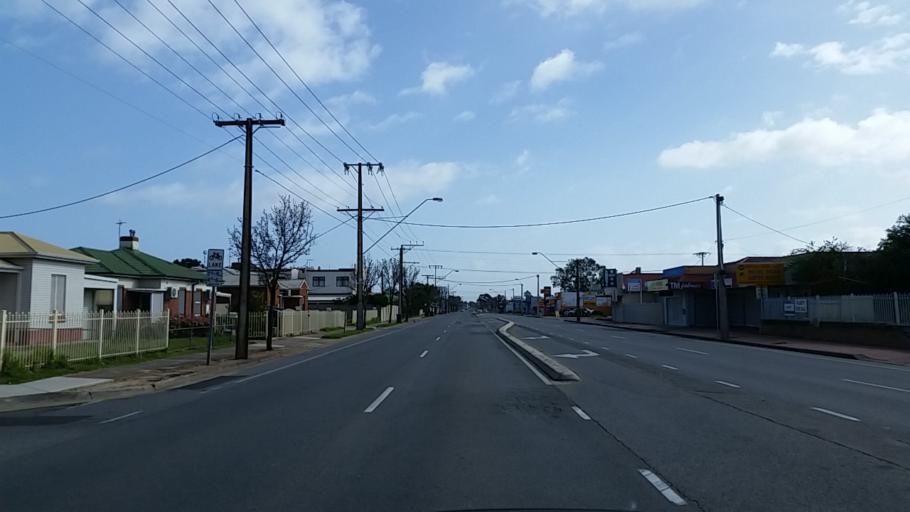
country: AU
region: South Australia
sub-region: Charles Sturt
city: Woodville North
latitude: -34.8687
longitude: 138.5479
